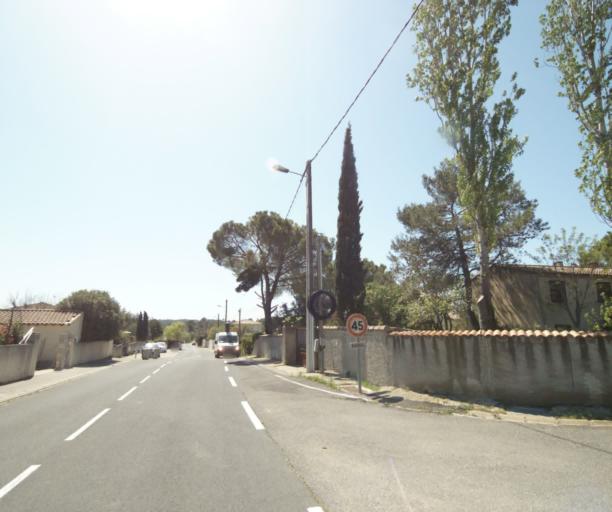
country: FR
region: Languedoc-Roussillon
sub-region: Departement de l'Herault
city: Sussargues
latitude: 43.7107
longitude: 4.0010
